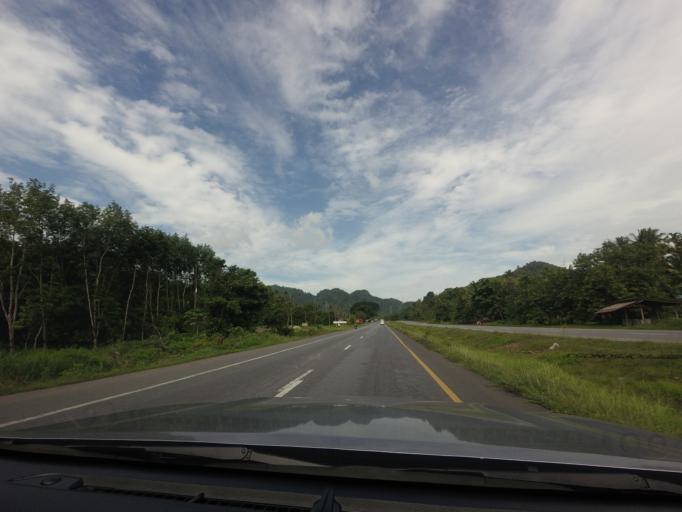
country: TH
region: Nakhon Si Thammarat
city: Ron Phibun
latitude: 8.1413
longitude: 99.7937
